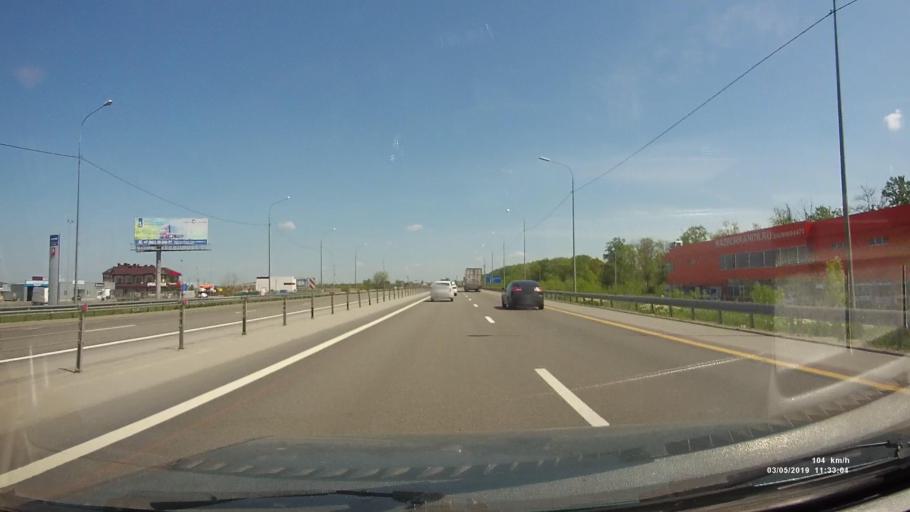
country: RU
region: Rostov
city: Ol'ginskaya
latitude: 47.1209
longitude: 39.8653
